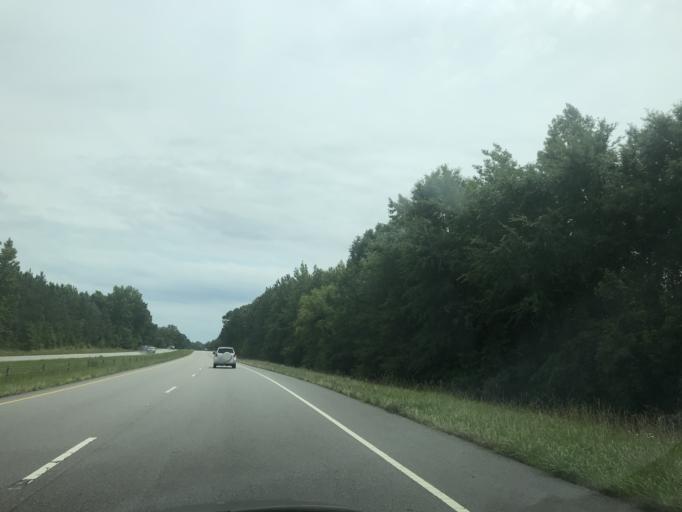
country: US
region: North Carolina
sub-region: Vance County
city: South Henderson
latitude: 36.2120
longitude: -78.4477
